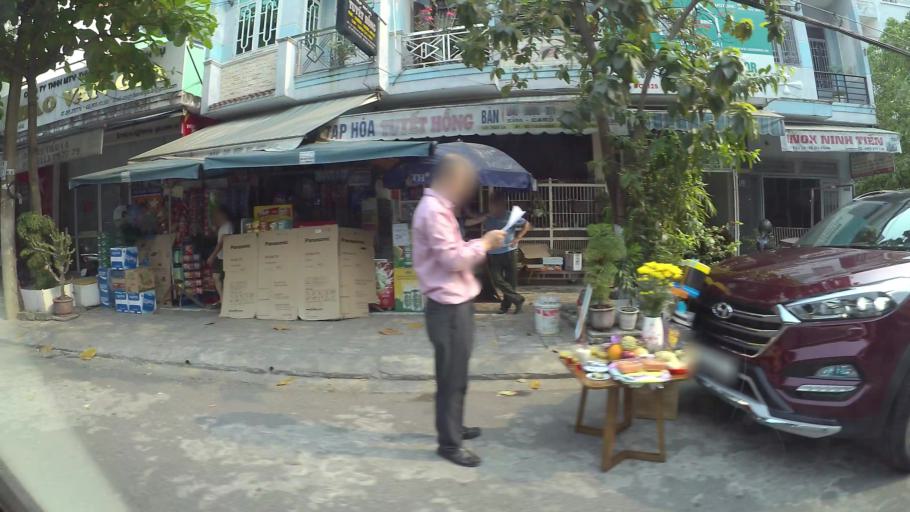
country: VN
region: Da Nang
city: Son Tra
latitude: 16.0449
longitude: 108.2178
